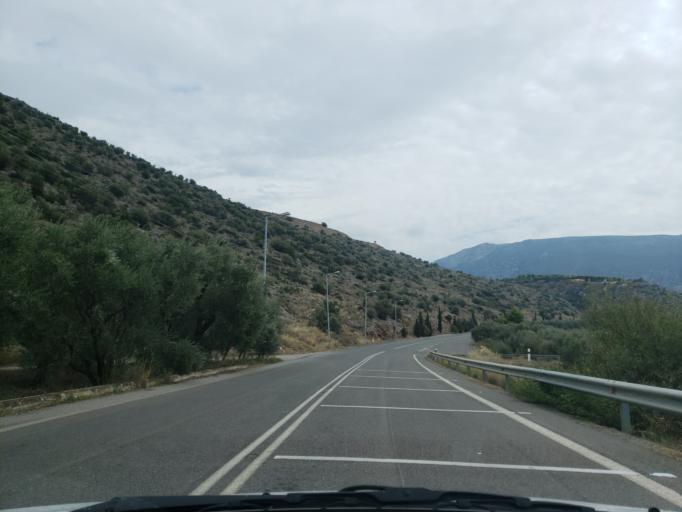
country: GR
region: Central Greece
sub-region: Nomos Fokidos
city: Delphi
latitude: 38.4776
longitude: 22.4513
